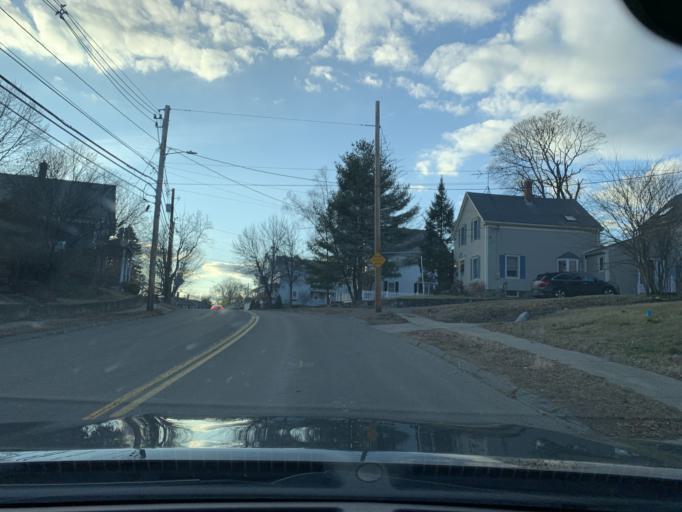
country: US
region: Massachusetts
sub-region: Essex County
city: Danvers
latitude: 42.5655
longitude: -70.9493
